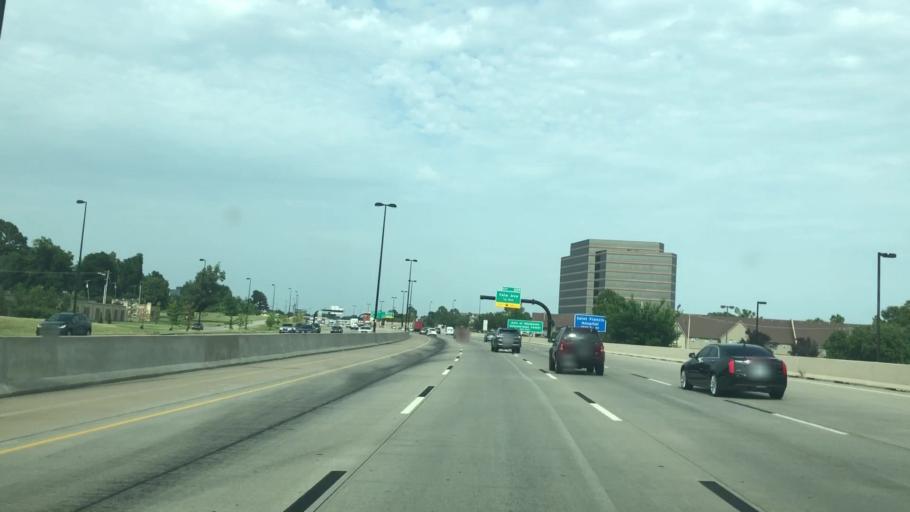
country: US
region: Oklahoma
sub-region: Tulsa County
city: Jenks
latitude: 36.0909
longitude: -95.9333
